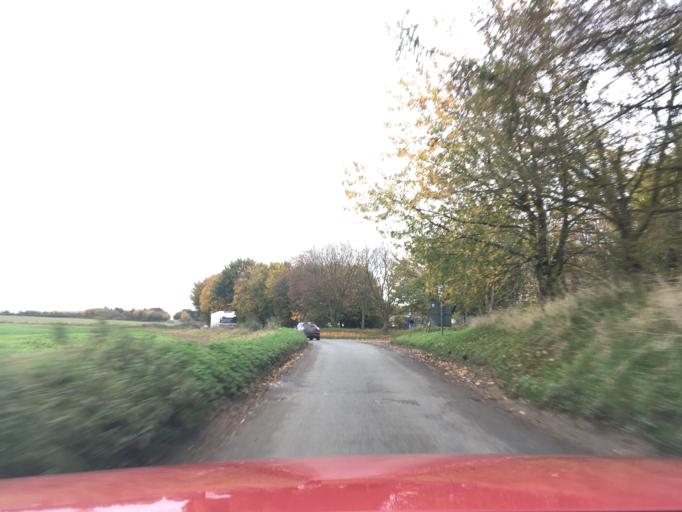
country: GB
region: England
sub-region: Somerset
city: South Petherton
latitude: 50.9406
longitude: -2.8463
